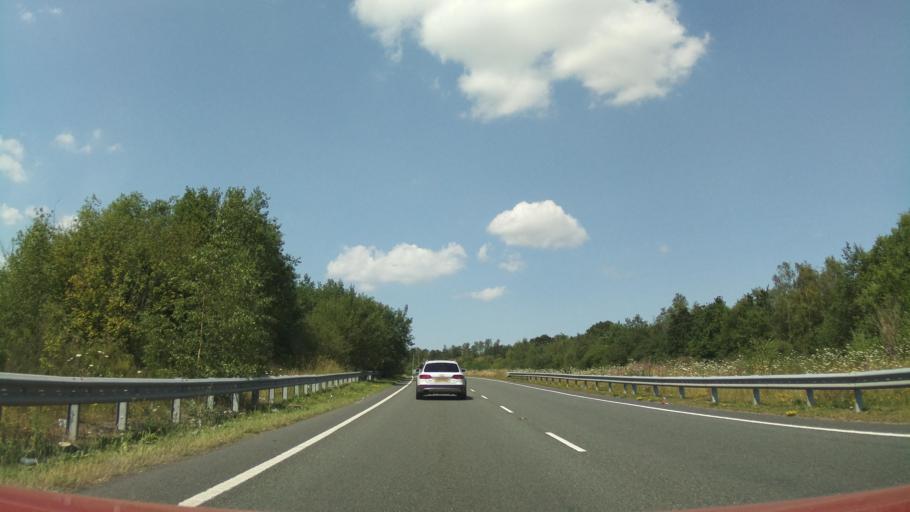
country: GB
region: Wales
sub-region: Caerphilly County Borough
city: Bargoed
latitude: 51.6803
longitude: -3.2226
